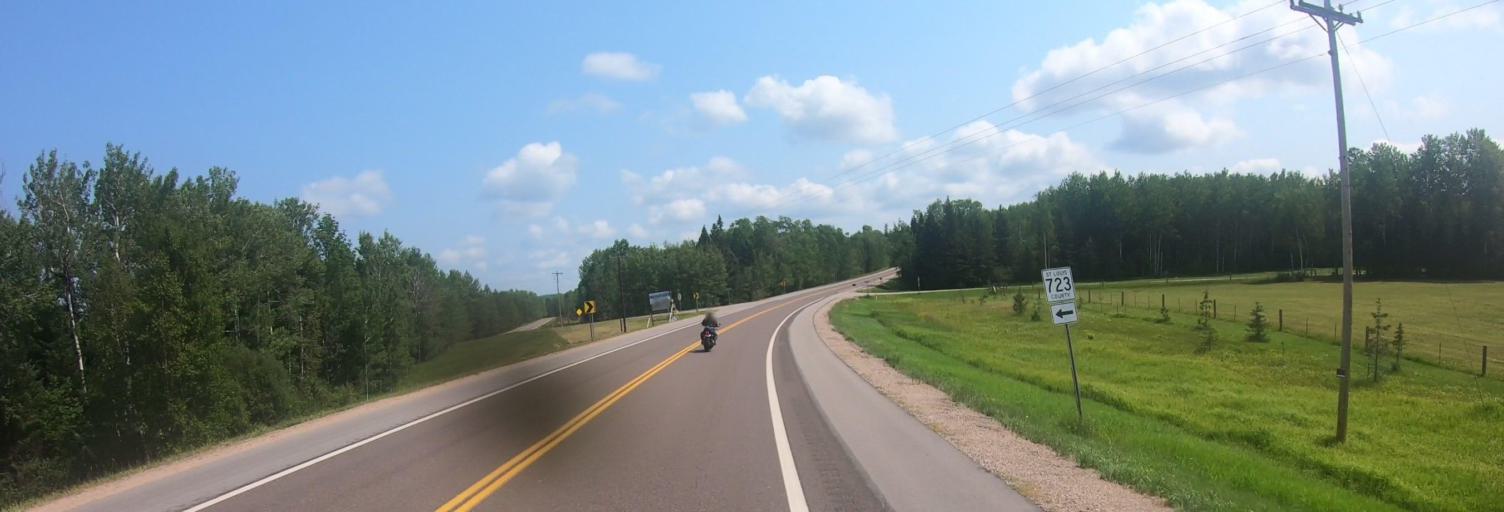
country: US
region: Minnesota
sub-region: Saint Louis County
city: Mountain Iron
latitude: 48.0750
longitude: -92.6766
